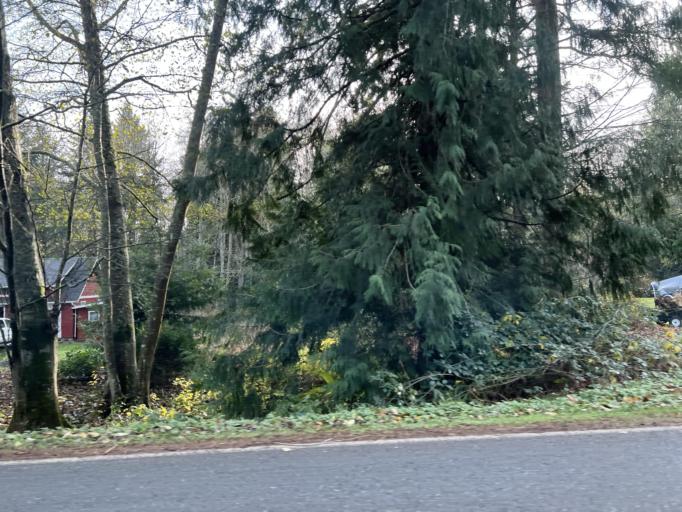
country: US
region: Washington
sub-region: Kitsap County
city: Bainbridge Island
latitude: 47.6647
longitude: -122.5120
